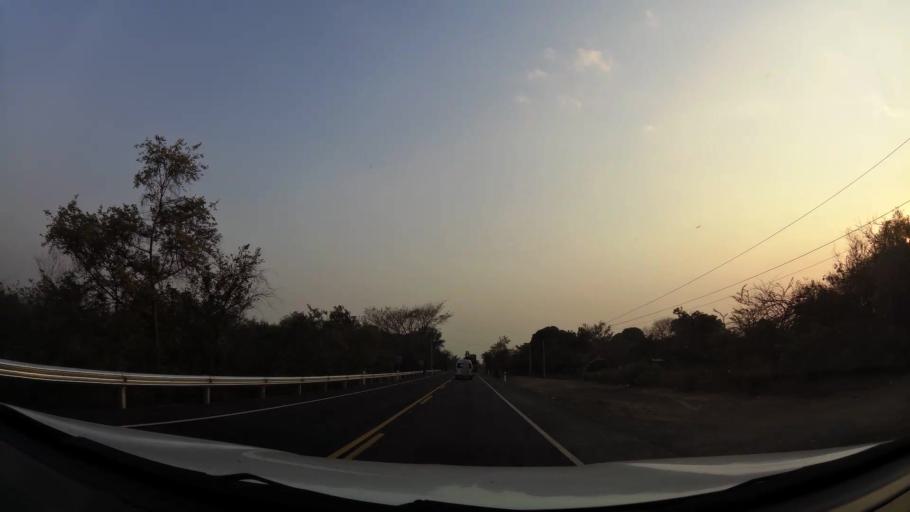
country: NI
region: Leon
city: La Paz Centro
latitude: 12.3291
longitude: -86.6851
